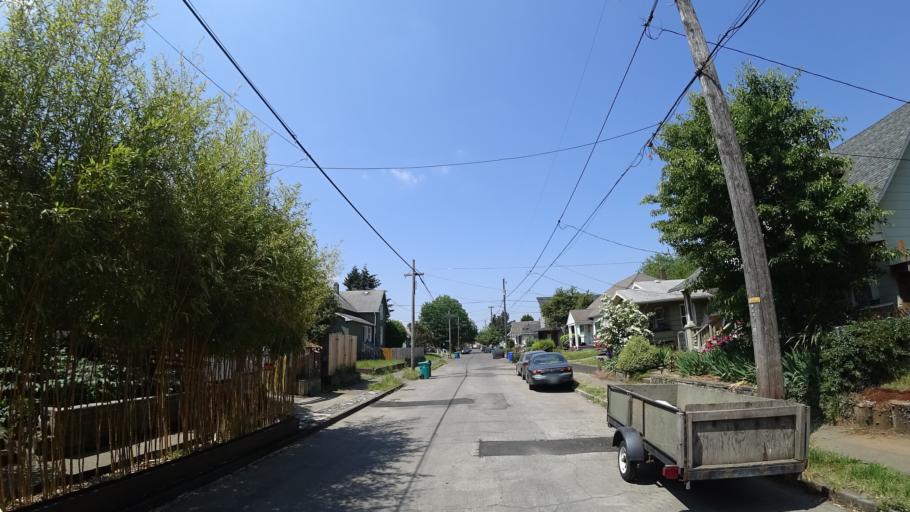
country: US
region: Oregon
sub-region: Multnomah County
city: Portland
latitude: 45.5618
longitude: -122.6574
